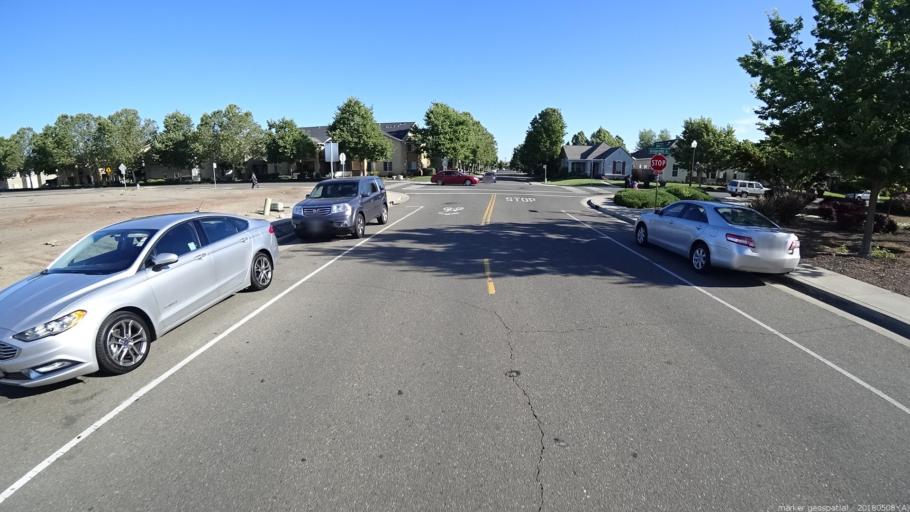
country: US
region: California
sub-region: Sacramento County
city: Elverta
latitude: 38.6816
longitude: -121.5054
